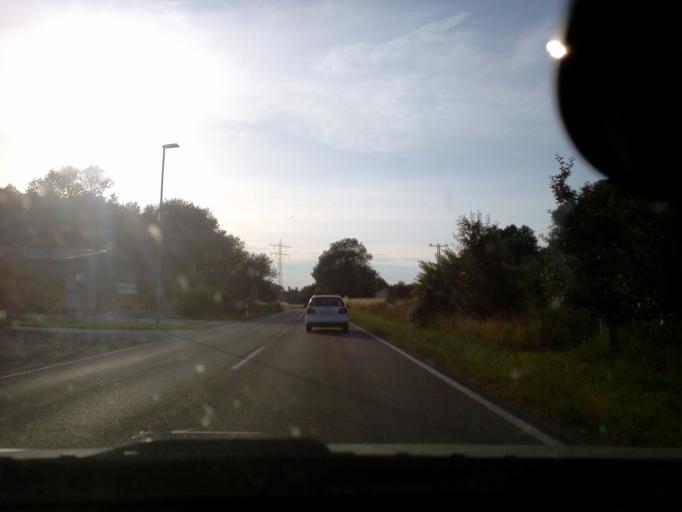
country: DE
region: Baden-Wuerttemberg
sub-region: Karlsruhe Region
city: Woessingen
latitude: 49.0186
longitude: 8.5969
